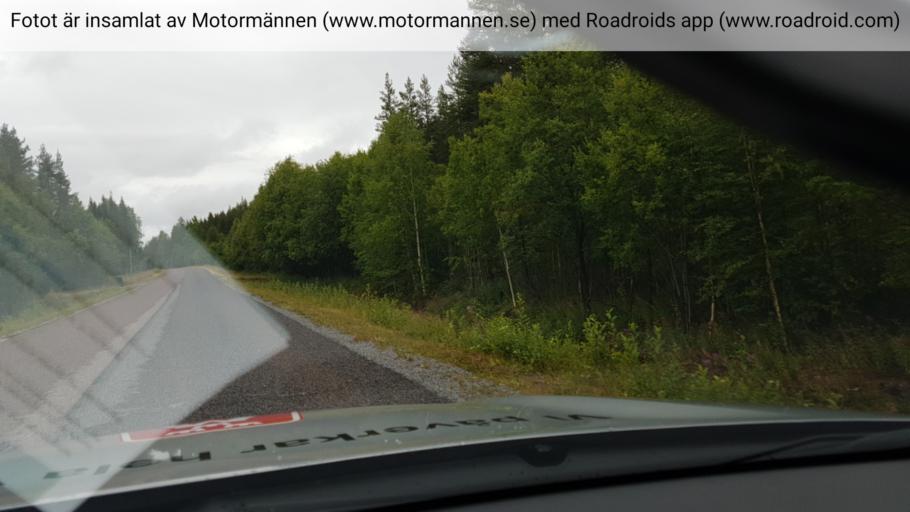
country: SE
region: Norrbotten
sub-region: Gallivare Kommun
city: Gaellivare
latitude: 66.5089
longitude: 20.5633
